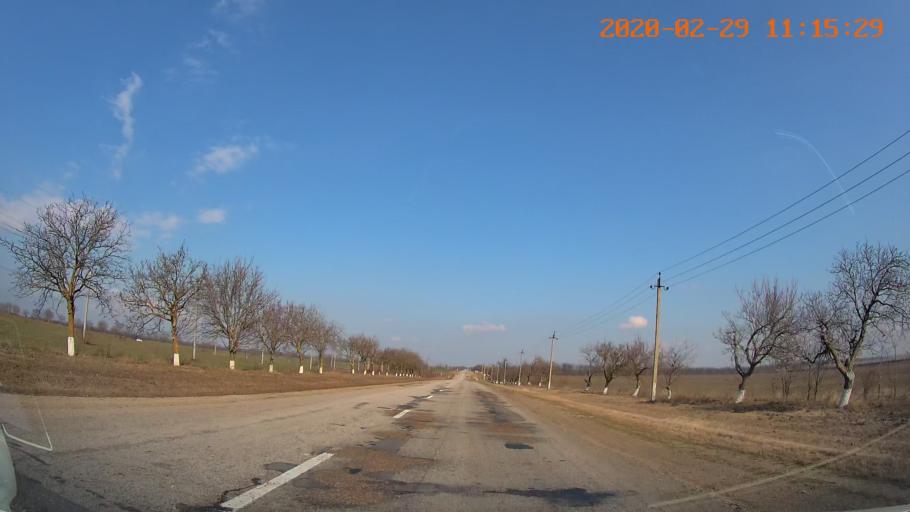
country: MD
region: Telenesti
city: Dubasari
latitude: 47.2953
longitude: 29.1652
